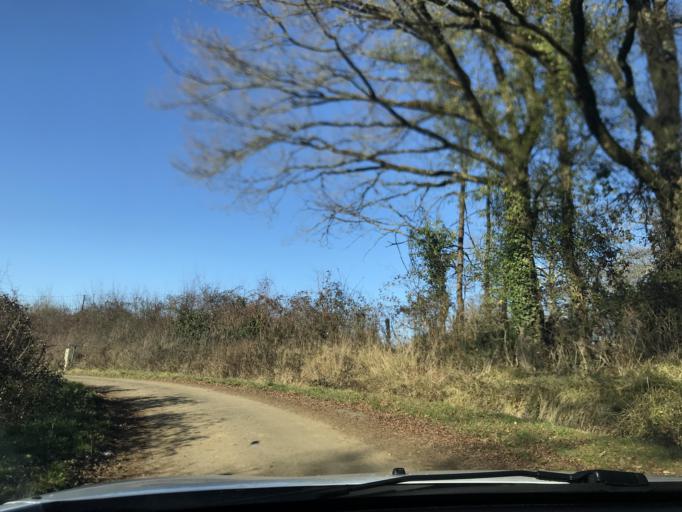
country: FR
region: Poitou-Charentes
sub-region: Departement de la Charente
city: Chasseneuil-sur-Bonnieure
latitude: 45.8431
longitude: 0.5189
